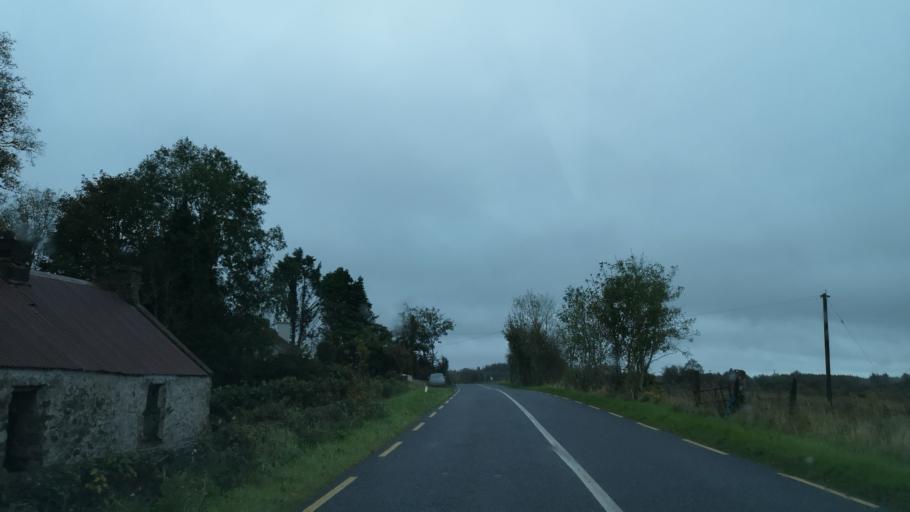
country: IE
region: Connaught
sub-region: Maigh Eo
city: Ballyhaunis
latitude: 53.7986
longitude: -8.7000
